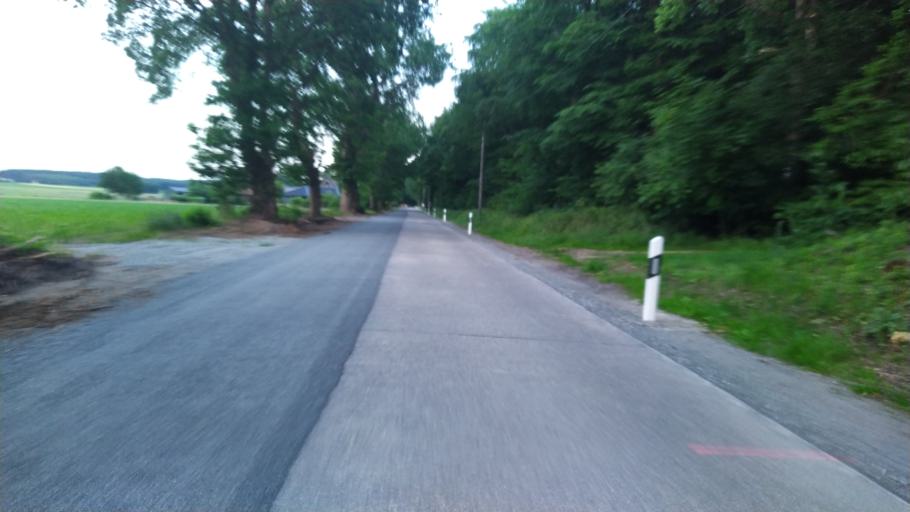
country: DE
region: Lower Saxony
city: Bremervorde
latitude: 53.4857
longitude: 9.1975
